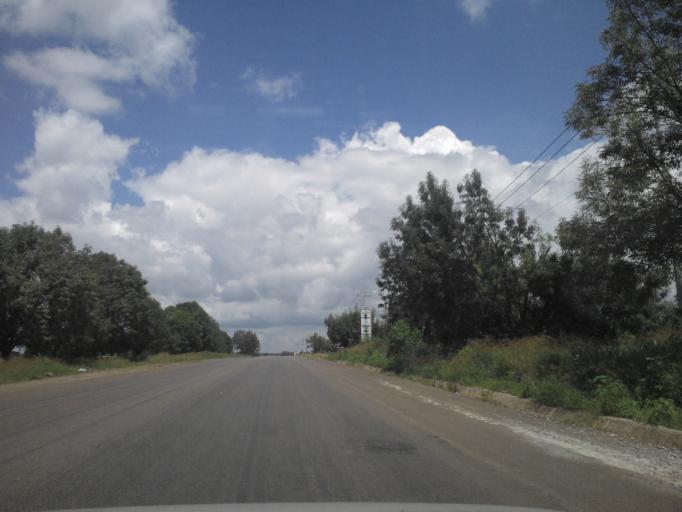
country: MX
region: Jalisco
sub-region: Atotonilco el Alto
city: Ojo de Agua de Moran
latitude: 20.5863
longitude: -102.4970
